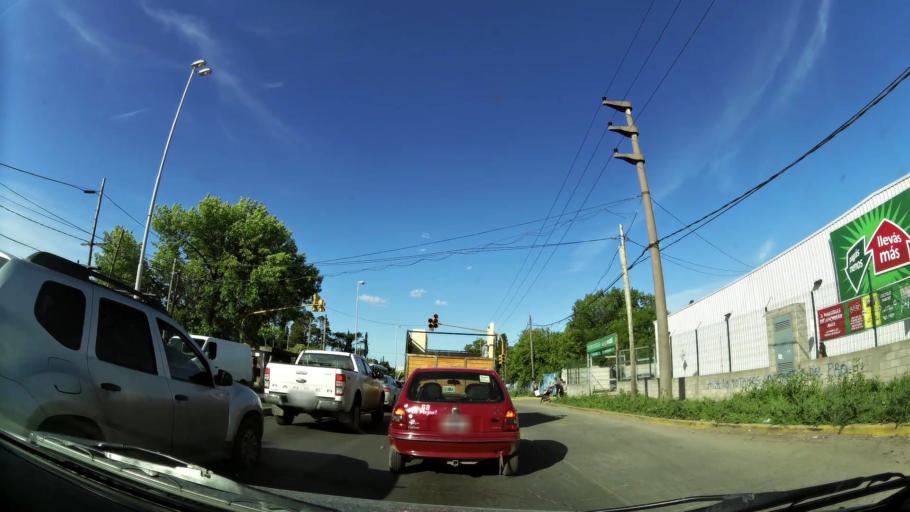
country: AR
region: Buenos Aires
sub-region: Partido de Almirante Brown
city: Adrogue
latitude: -34.8090
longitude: -58.3438
